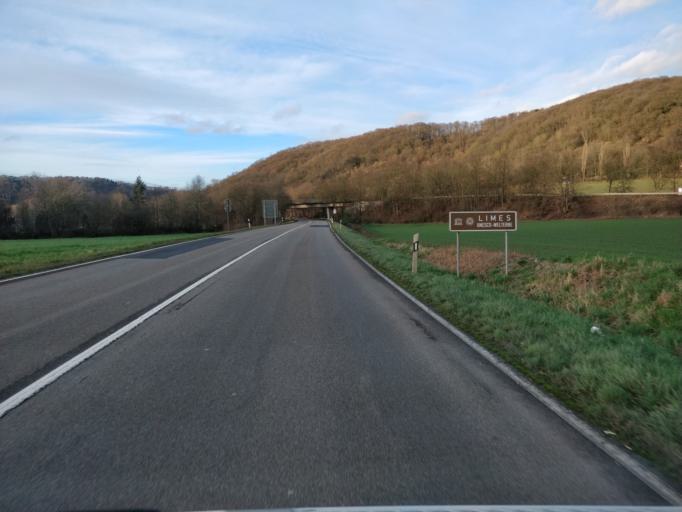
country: DE
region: Rheinland-Pfalz
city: Rheinbrohl
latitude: 50.5099
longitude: 7.3254
